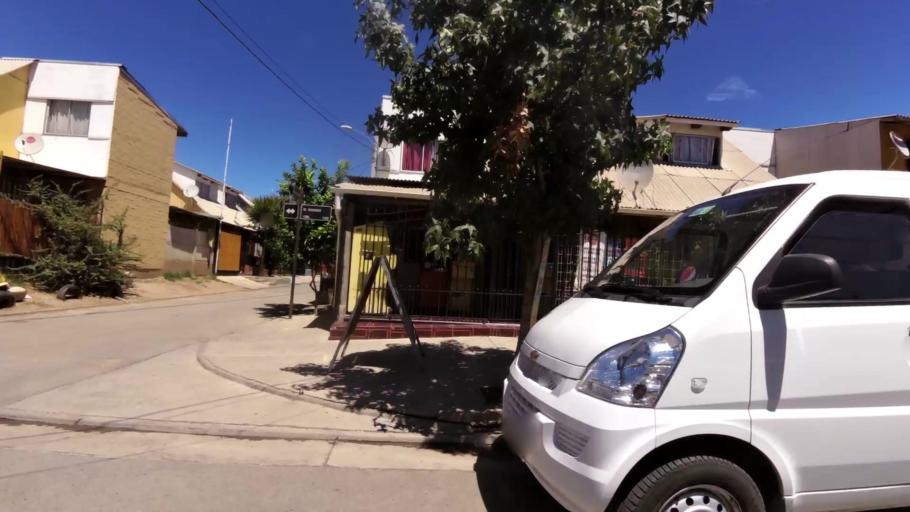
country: CL
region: O'Higgins
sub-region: Provincia de Cachapoal
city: Machali
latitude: -34.1638
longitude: -70.6954
